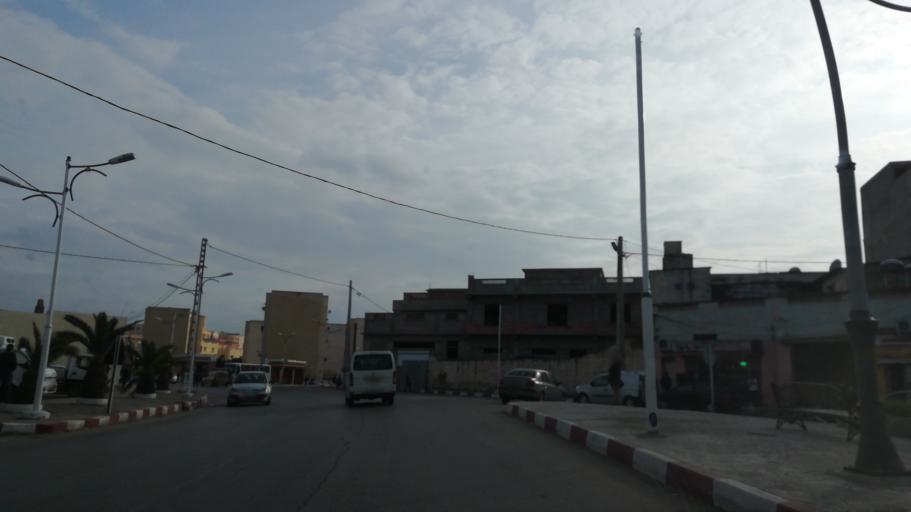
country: DZ
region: Mostaganem
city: Mostaganem
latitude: 35.8972
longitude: 0.0741
